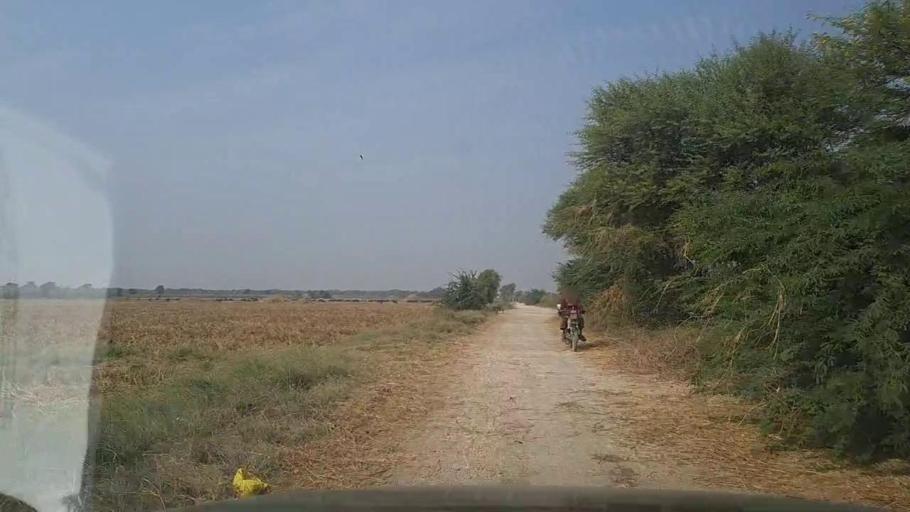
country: PK
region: Sindh
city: Bulri
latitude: 24.9732
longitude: 68.3067
